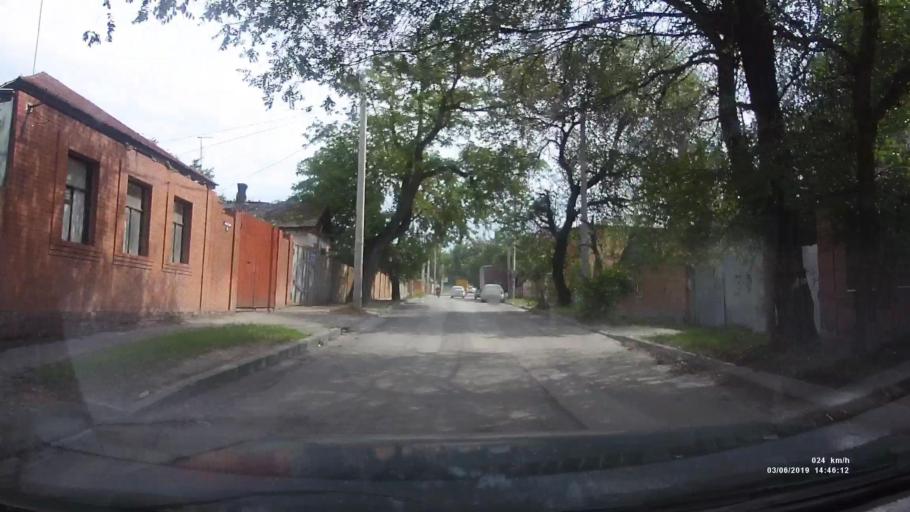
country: RU
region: Rostov
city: Rostov-na-Donu
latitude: 47.2457
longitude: 39.7240
